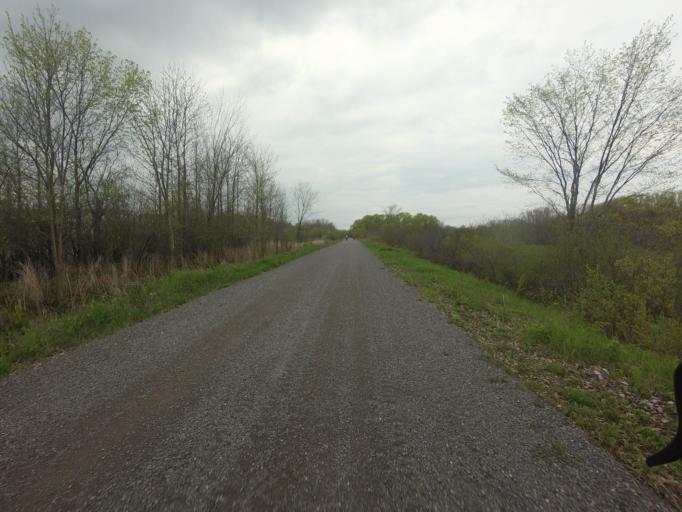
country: CA
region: Ontario
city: Carleton Place
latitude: 45.2189
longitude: -76.1855
